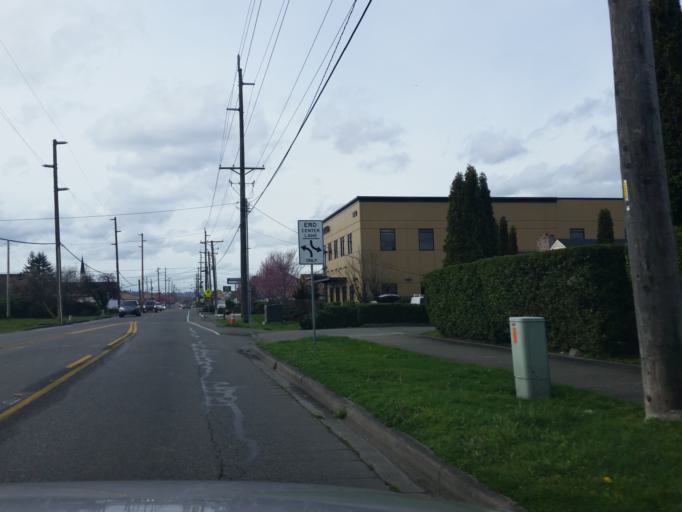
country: US
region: Washington
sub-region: Pierce County
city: Fife
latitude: 47.2390
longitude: -122.3442
